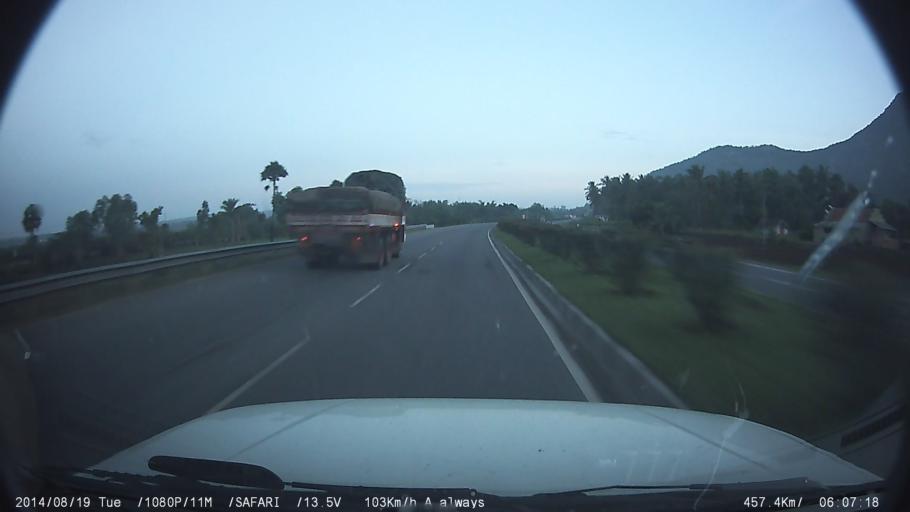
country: IN
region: Tamil Nadu
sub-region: Salem
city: Omalur
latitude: 11.8984
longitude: 78.0635
